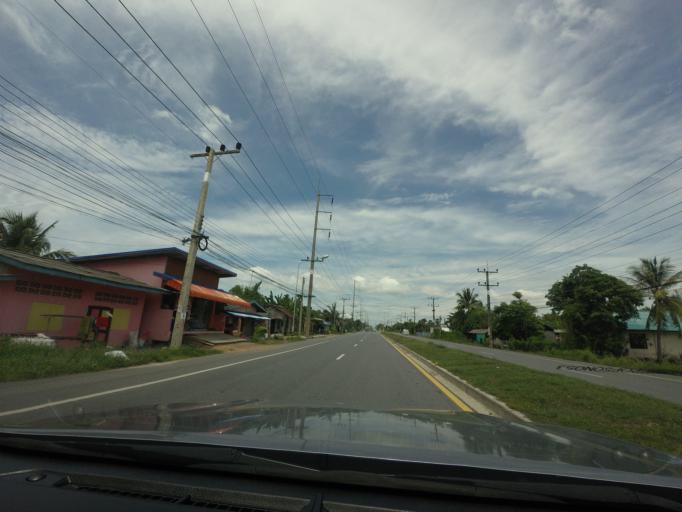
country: TH
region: Songkhla
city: Krasae Sin
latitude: 7.6923
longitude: 100.3773
